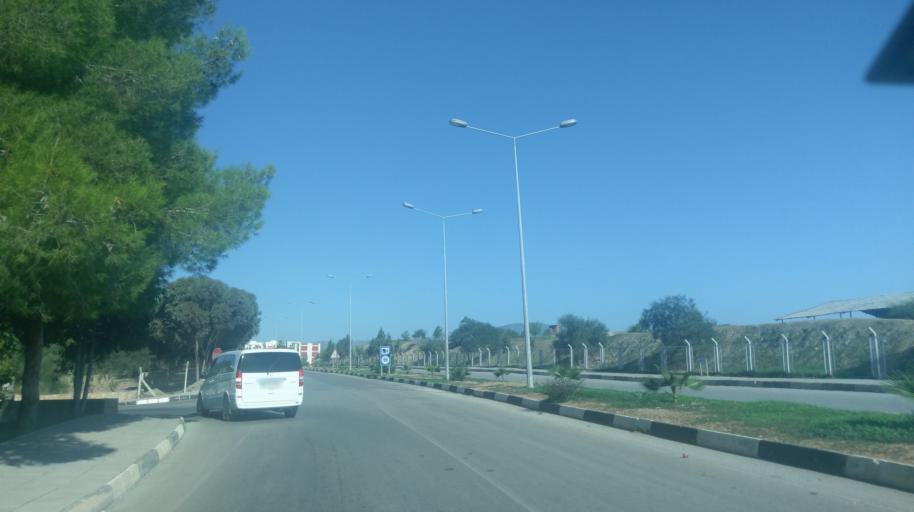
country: CY
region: Lefkosia
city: Nicosia
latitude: 35.2256
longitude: 33.3277
